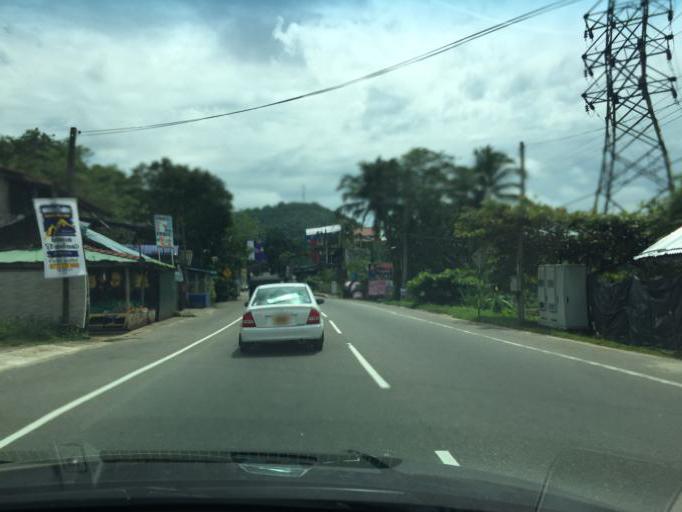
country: LK
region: Western
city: Horana South
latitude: 6.7229
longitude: 80.0413
